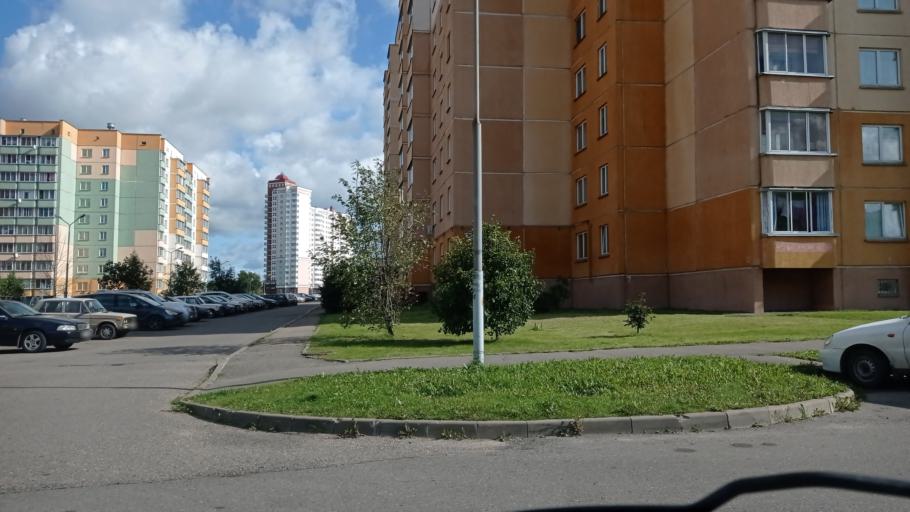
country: BY
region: Vitebsk
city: Vitebsk
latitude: 55.1708
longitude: 30.2639
